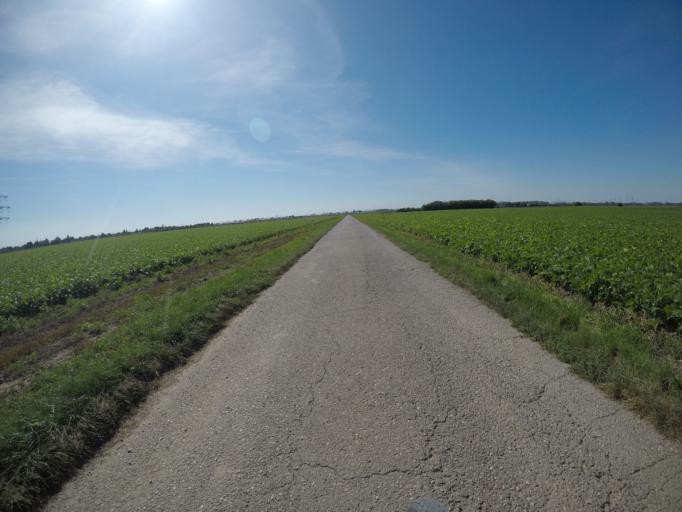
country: DE
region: Hesse
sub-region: Regierungsbezirk Darmstadt
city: Biblis
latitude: 49.6702
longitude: 8.4142
